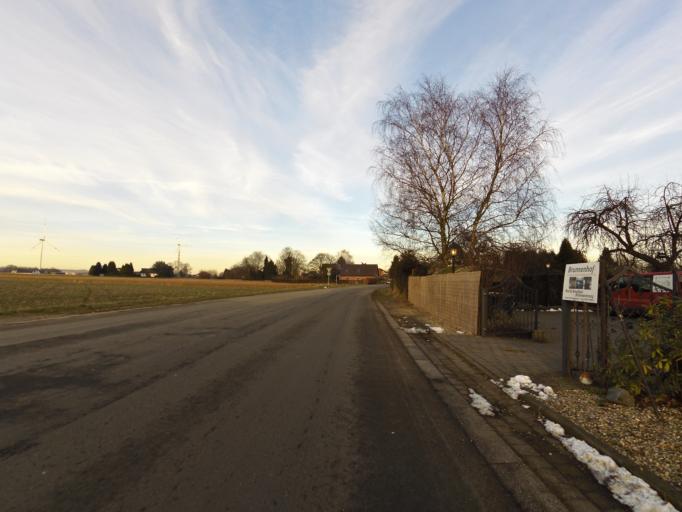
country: DE
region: North Rhine-Westphalia
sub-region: Regierungsbezirk Dusseldorf
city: Emmerich
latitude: 51.8510
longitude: 6.2582
